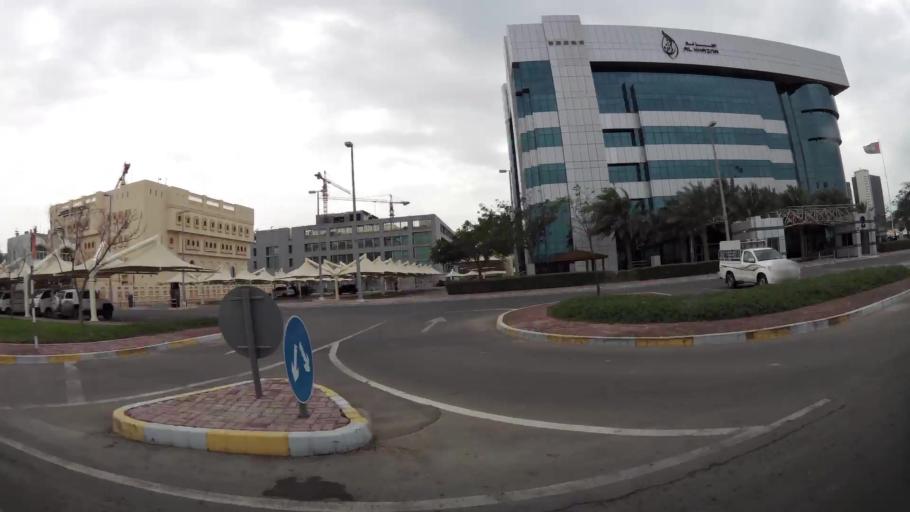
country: AE
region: Abu Dhabi
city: Abu Dhabi
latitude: 24.4233
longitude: 54.4484
